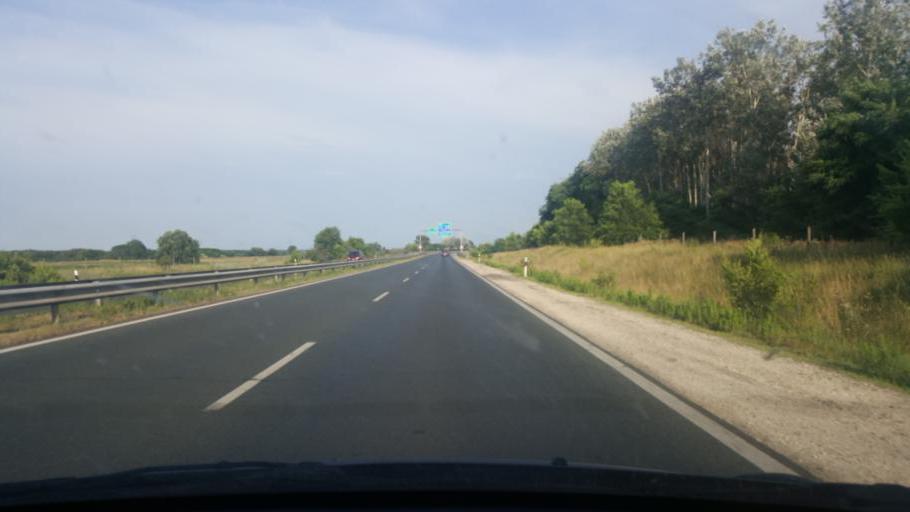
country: HU
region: Pest
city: Vecses
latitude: 47.4144
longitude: 19.2859
